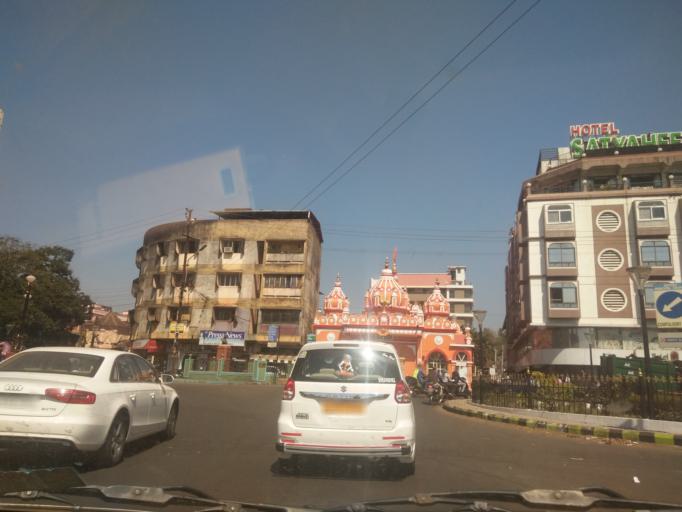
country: IN
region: Goa
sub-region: North Goa
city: Mapuca
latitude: 15.5907
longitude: 73.8101
